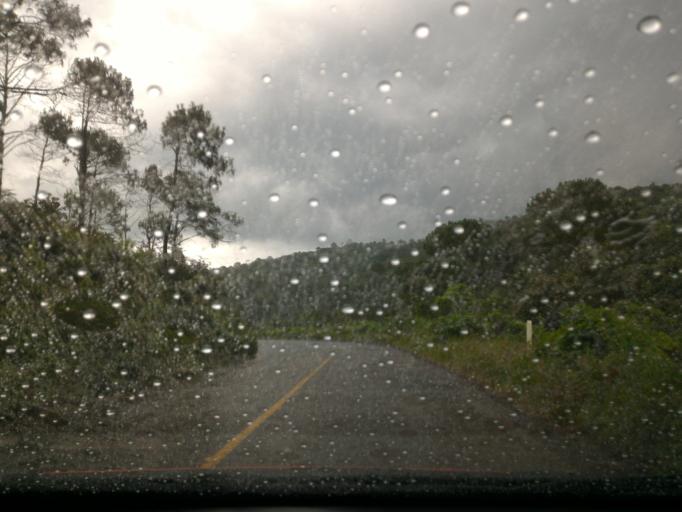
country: MX
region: Jalisco
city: San Andres Ixtlan
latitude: 19.8436
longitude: -103.4567
